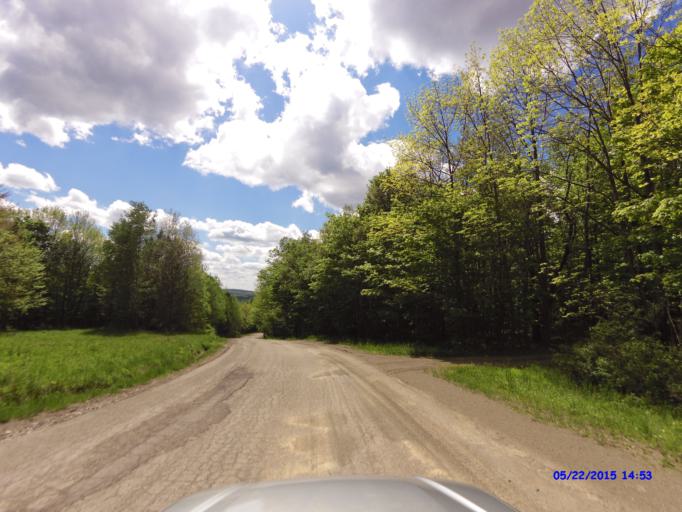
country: US
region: New York
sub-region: Cattaraugus County
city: Franklinville
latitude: 42.3818
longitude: -78.5809
